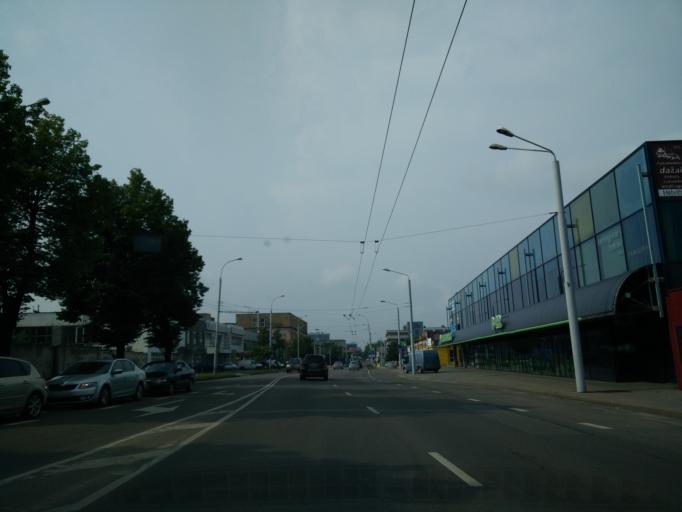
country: LT
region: Vilnius County
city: Naujamiestis
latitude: 54.6696
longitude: 25.2704
